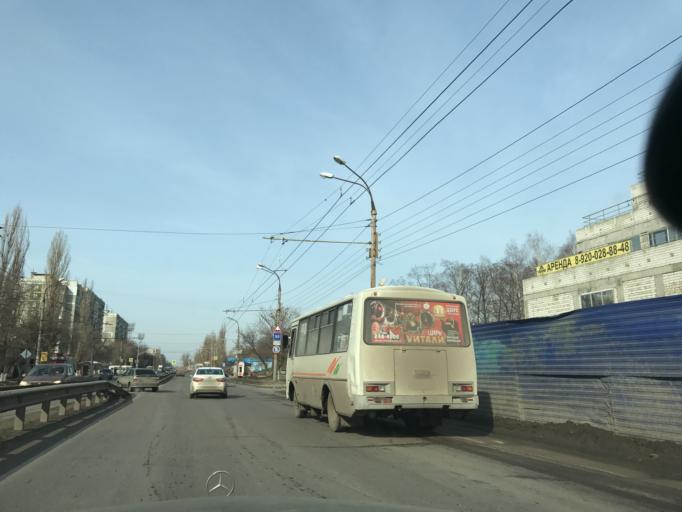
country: RU
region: Nizjnij Novgorod
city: Nizhniy Novgorod
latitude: 56.2632
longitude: 43.8963
